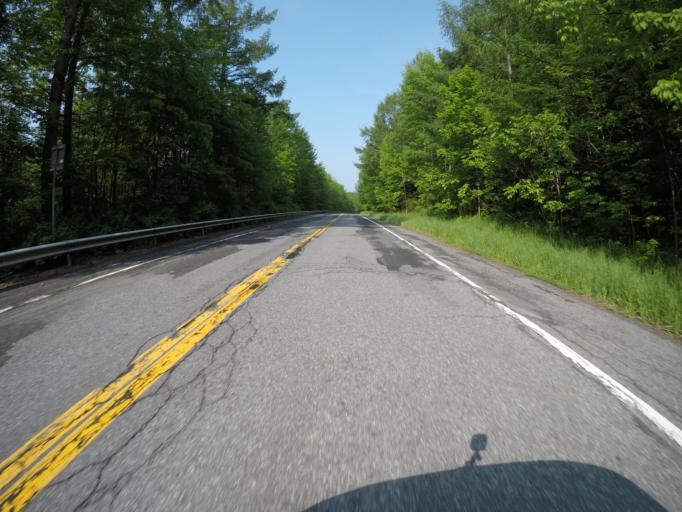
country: US
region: New York
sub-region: Delaware County
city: Delhi
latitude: 42.1183
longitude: -74.7597
